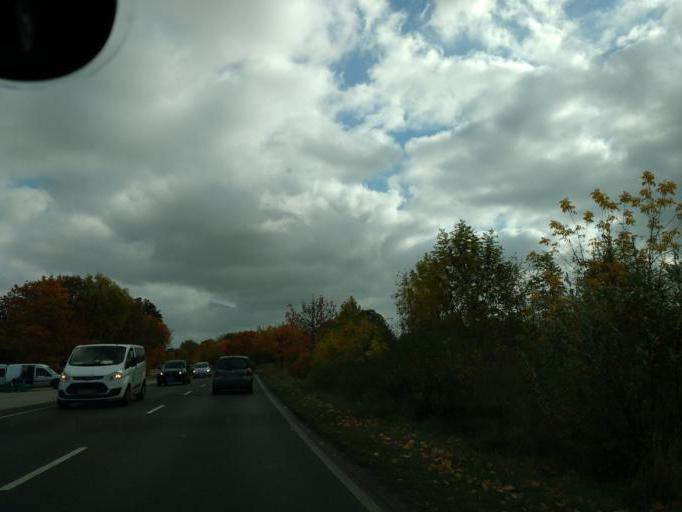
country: DE
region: Berlin
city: Hellersdorf
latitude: 52.5429
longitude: 13.6340
